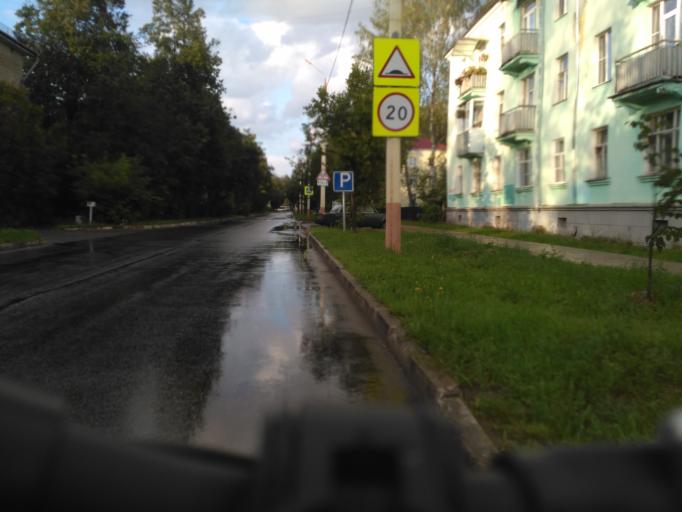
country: RU
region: Moskovskaya
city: Dubna
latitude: 56.7477
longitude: 37.2004
